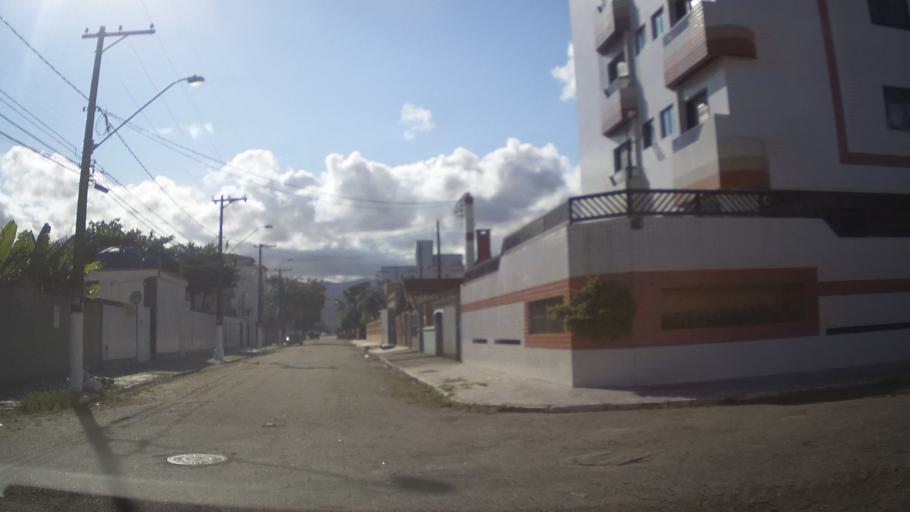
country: BR
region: Sao Paulo
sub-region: Praia Grande
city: Praia Grande
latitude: -24.0291
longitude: -46.4830
